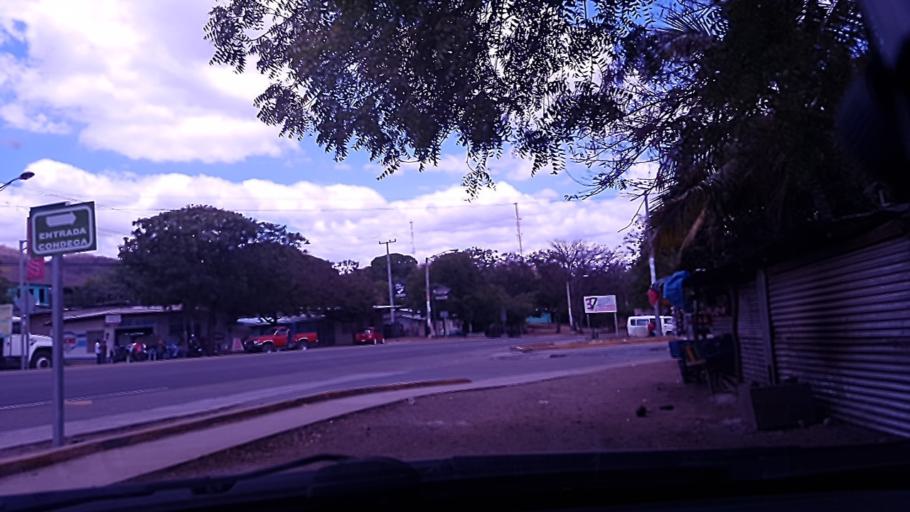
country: NI
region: Esteli
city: Condega
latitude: 13.3609
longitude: -86.4009
